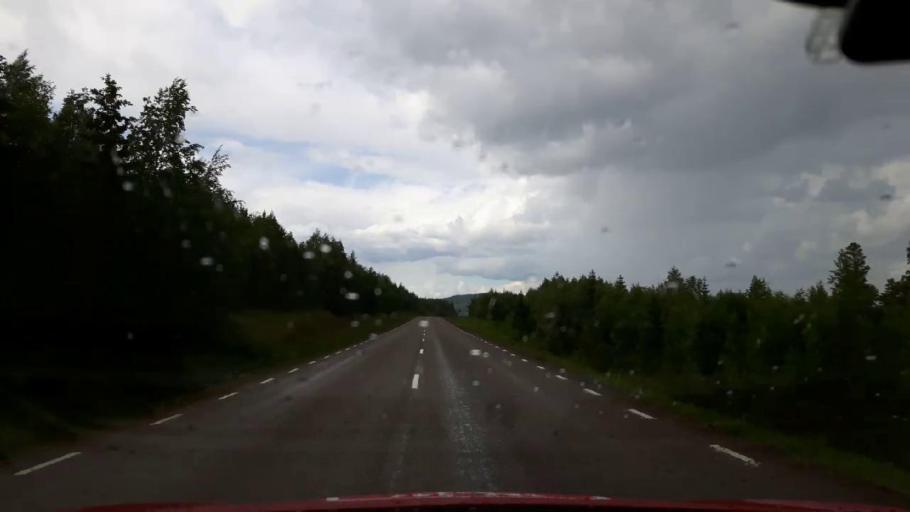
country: SE
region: Jaemtland
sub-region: Krokoms Kommun
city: Valla
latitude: 63.8905
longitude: 14.2702
